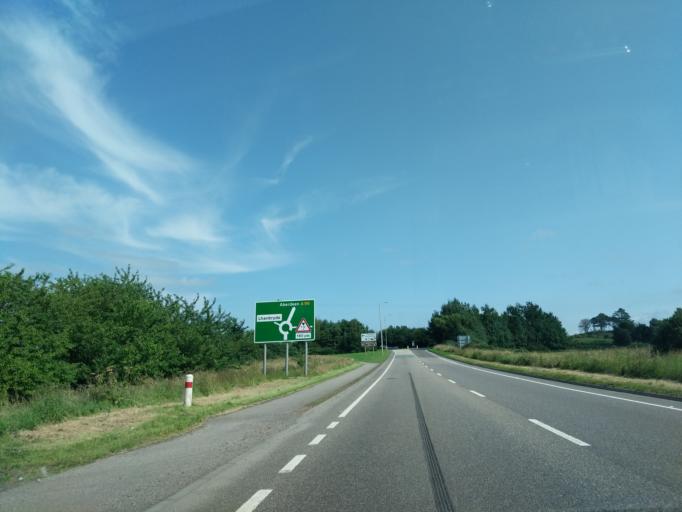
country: GB
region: Scotland
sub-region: Moray
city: Lhanbryd
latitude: 57.6363
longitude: -3.2370
